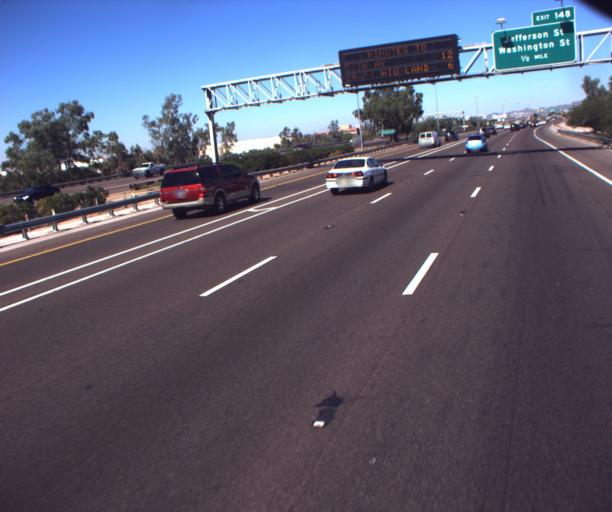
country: US
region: Arizona
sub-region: Maricopa County
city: Phoenix
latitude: 33.4354
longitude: -112.0374
